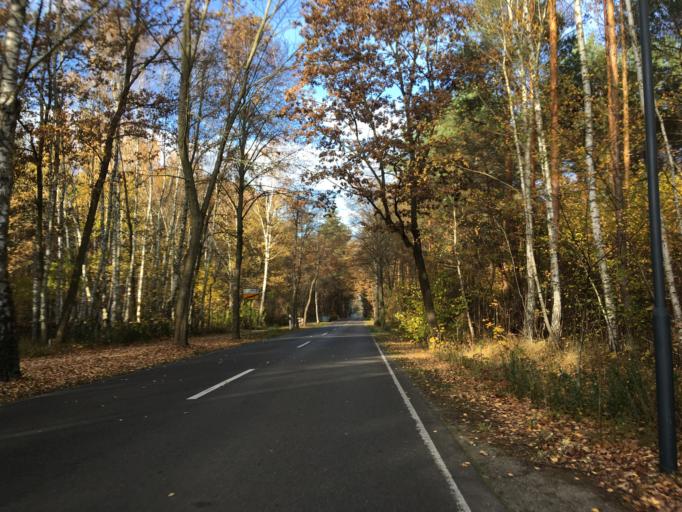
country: DE
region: Brandenburg
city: Gross Koris
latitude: 52.1533
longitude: 13.6772
